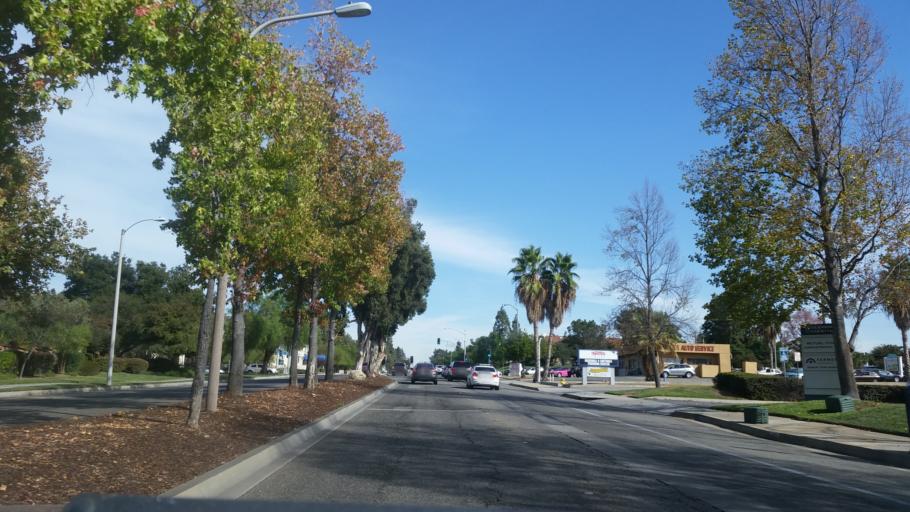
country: US
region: California
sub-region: Los Angeles County
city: San Dimas
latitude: 34.1272
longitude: -117.8217
